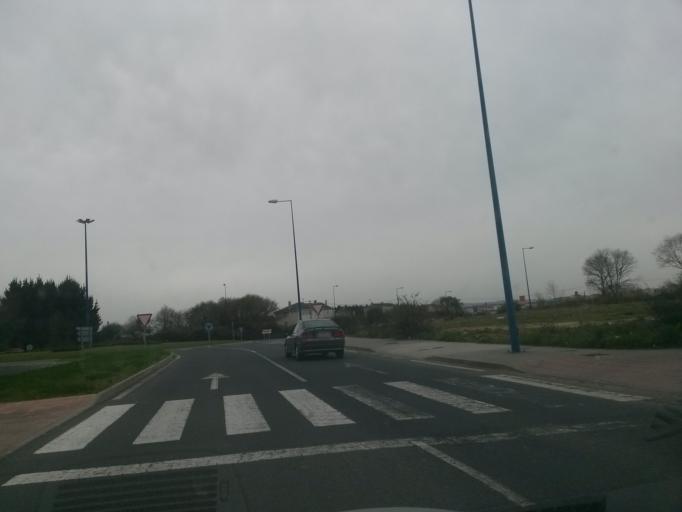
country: ES
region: Galicia
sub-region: Provincia de Lugo
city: Lugo
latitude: 43.0352
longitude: -7.5553
